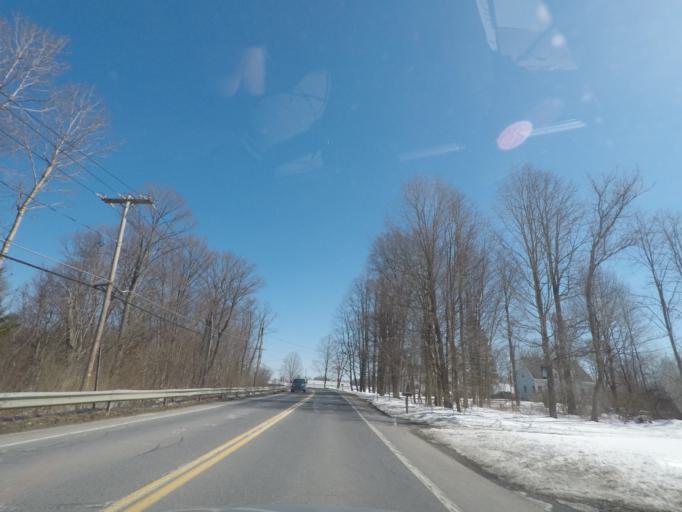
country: US
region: New York
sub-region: Saratoga County
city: Stillwater
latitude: 42.9047
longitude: -73.5966
